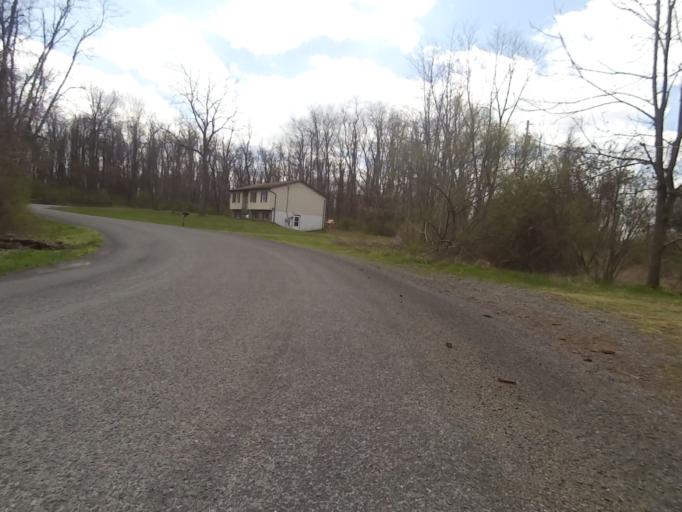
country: US
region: Pennsylvania
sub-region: Centre County
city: Houserville
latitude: 40.8625
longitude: -77.8230
